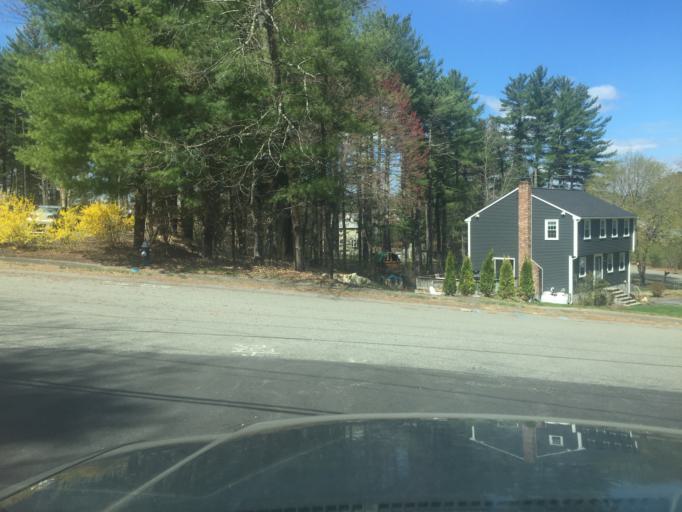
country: US
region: Massachusetts
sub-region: Norfolk County
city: Medway
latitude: 42.1726
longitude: -71.4037
